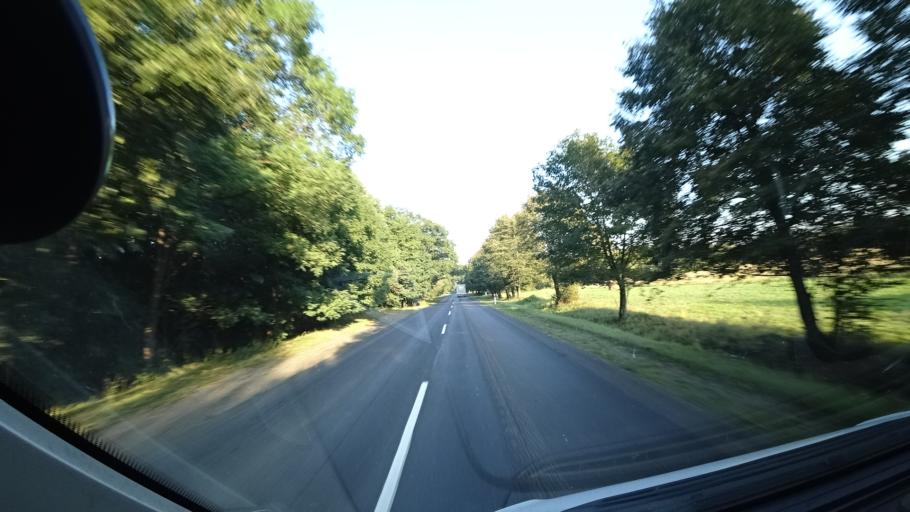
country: PL
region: Opole Voivodeship
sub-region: Powiat kedzierzynsko-kozielski
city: Dziergowice
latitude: 50.2812
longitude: 18.3315
